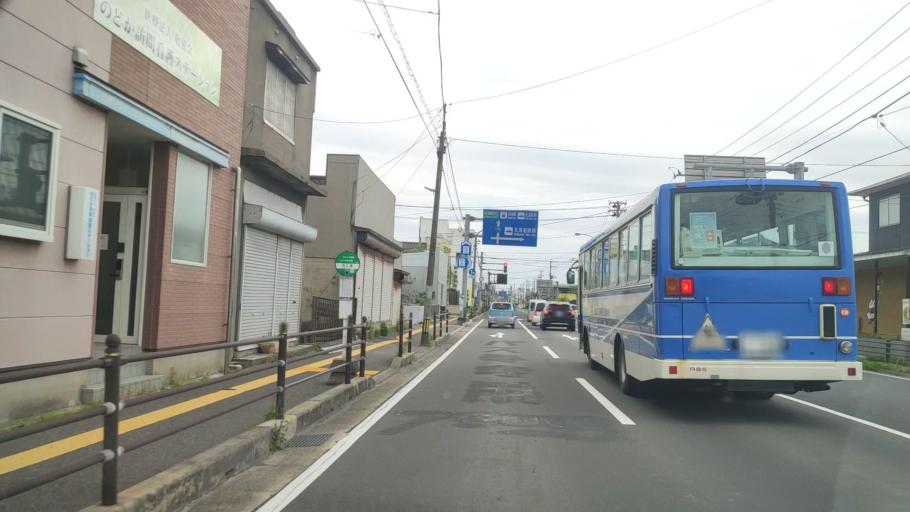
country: JP
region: Niigata
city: Niigata-shi
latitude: 37.9370
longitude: 139.0722
